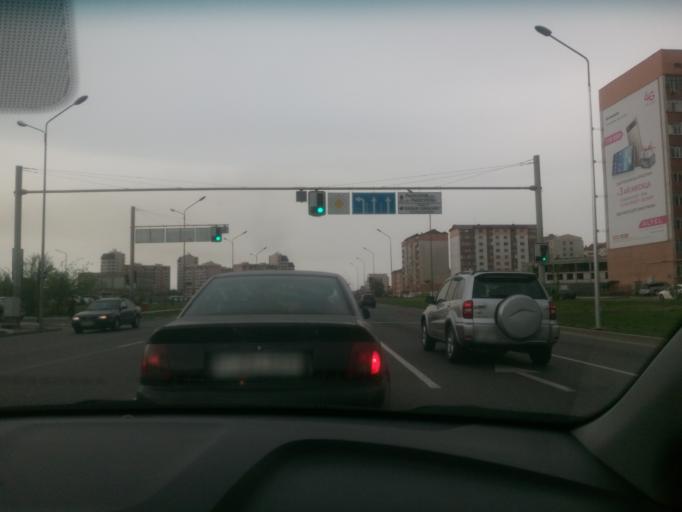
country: KZ
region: Almaty Qalasy
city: Almaty
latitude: 43.2499
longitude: 76.8250
